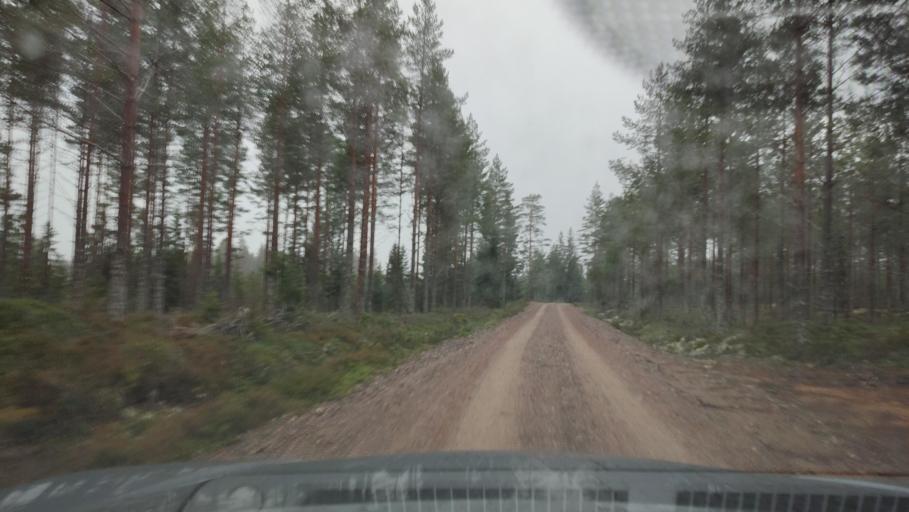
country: FI
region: Southern Ostrobothnia
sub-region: Suupohja
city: Karijoki
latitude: 62.1901
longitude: 21.7442
